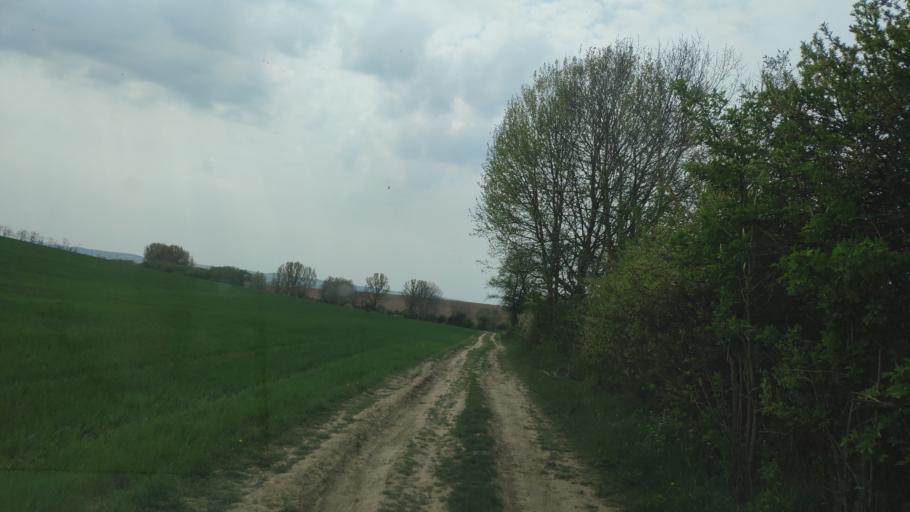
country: SK
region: Kosicky
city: Moldava nad Bodvou
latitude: 48.6169
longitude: 21.0402
